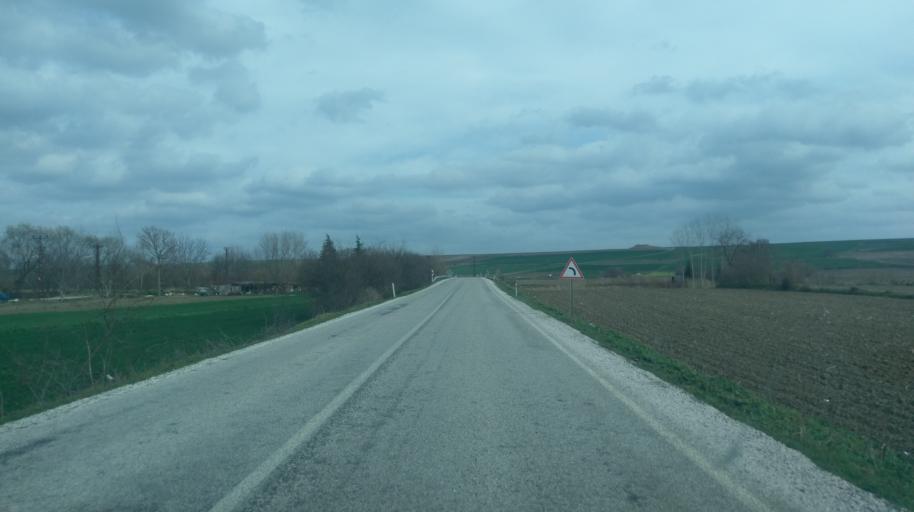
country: TR
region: Edirne
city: Haskoy
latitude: 41.6423
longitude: 26.8619
